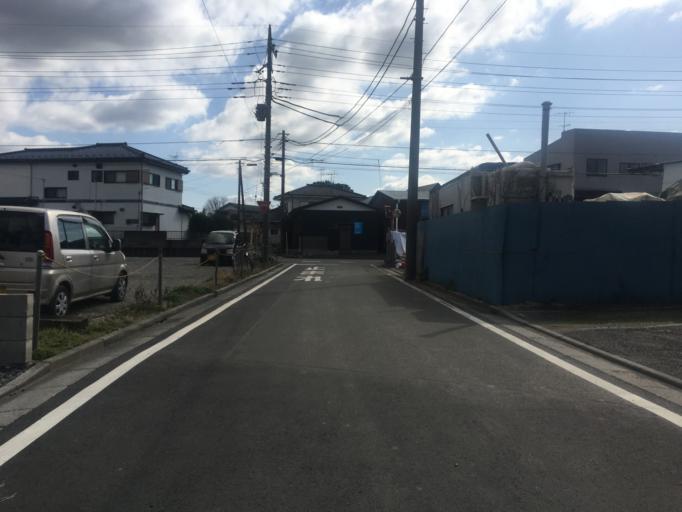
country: JP
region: Saitama
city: Yono
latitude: 35.8728
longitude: 139.5951
